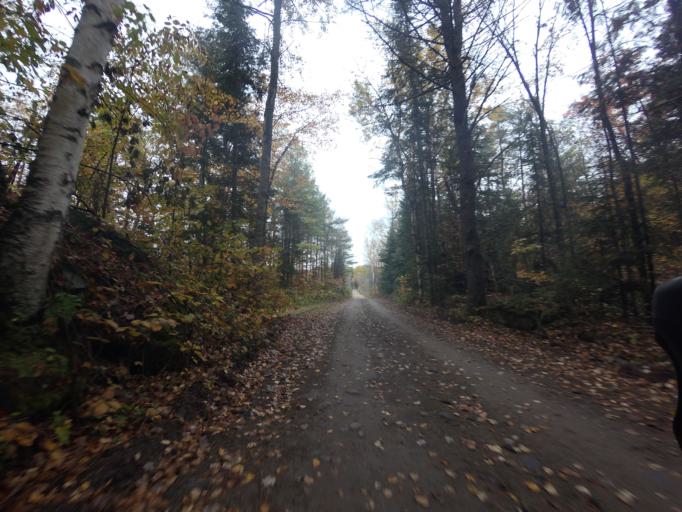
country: CA
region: Ontario
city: Renfrew
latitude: 45.1820
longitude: -76.6844
